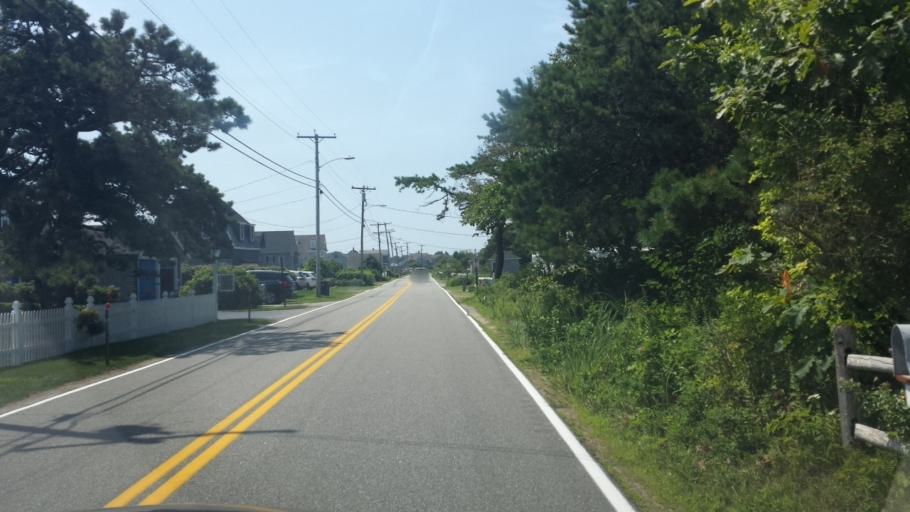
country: US
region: Maine
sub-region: York County
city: Old Orchard Beach
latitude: 43.4325
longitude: -70.3734
